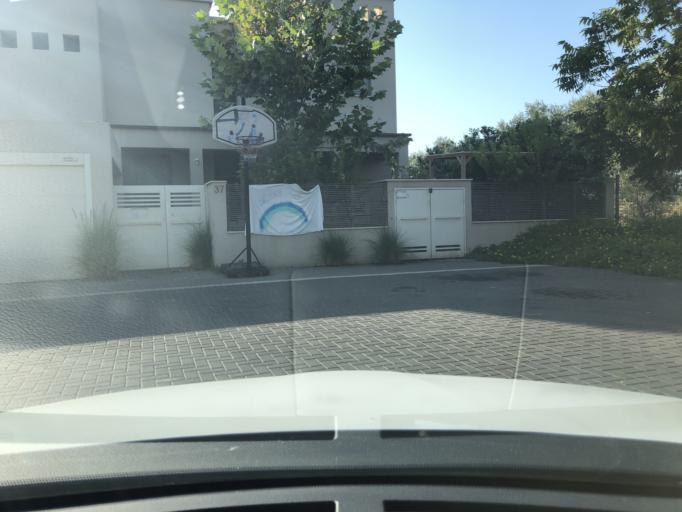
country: IL
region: Central District
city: Hod HaSharon
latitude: 32.1394
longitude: 34.9103
